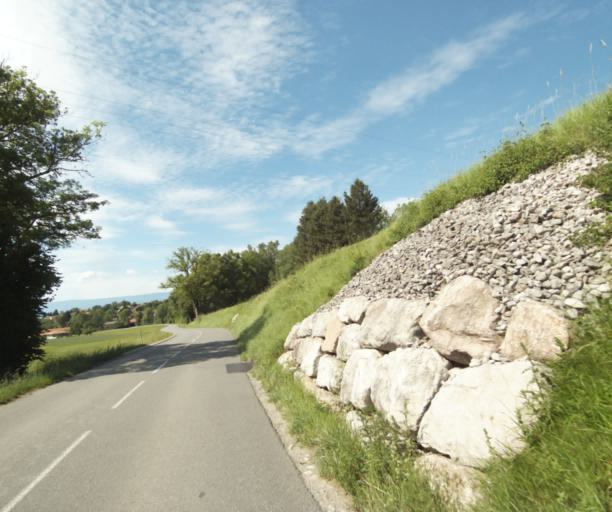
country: FR
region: Rhone-Alpes
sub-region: Departement de la Haute-Savoie
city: Perrignier
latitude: 46.3002
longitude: 6.4493
